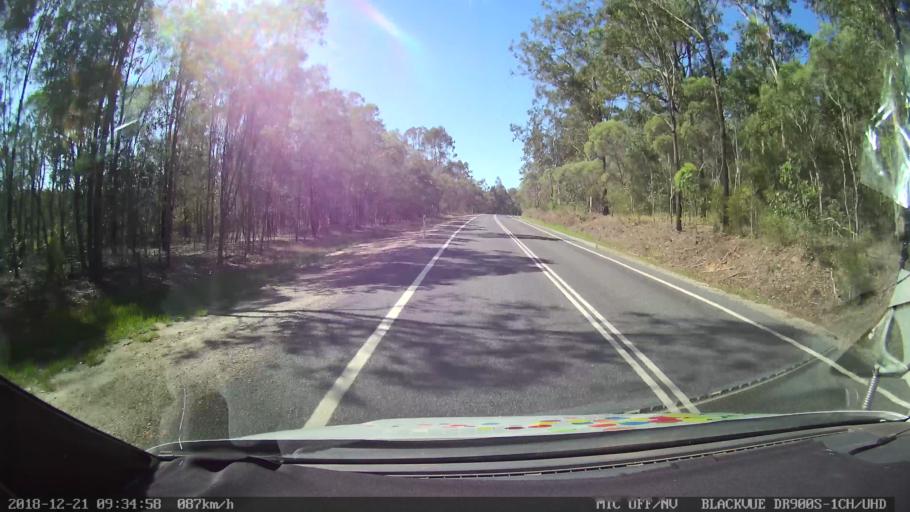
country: AU
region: New South Wales
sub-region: Clarence Valley
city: Grafton
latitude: -29.5045
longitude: 152.9821
